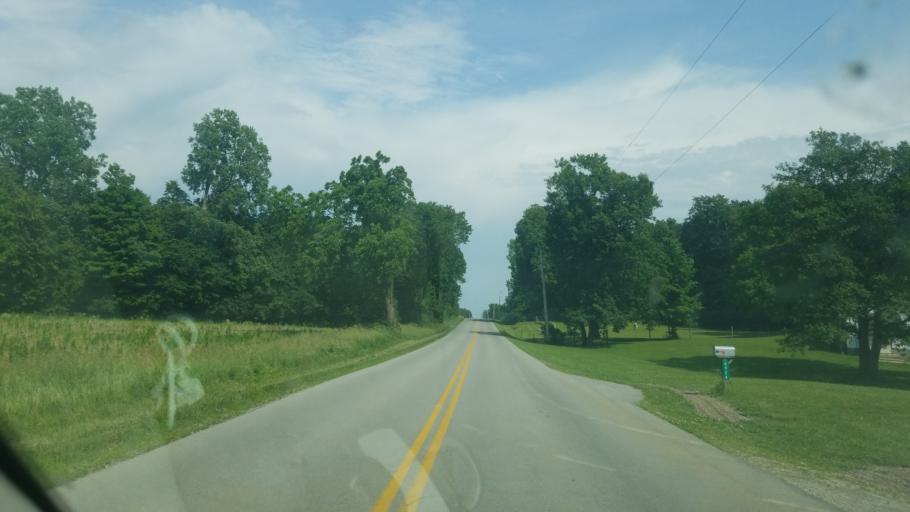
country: US
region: Ohio
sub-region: Logan County
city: West Liberty
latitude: 40.2990
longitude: -83.6510
